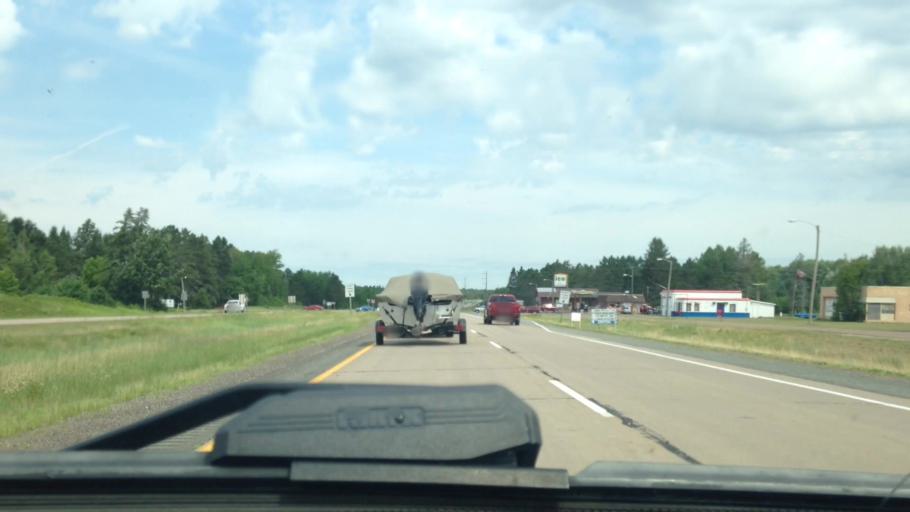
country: US
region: Wisconsin
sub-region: Douglas County
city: Lake Nebagamon
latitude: 46.2427
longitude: -91.8009
